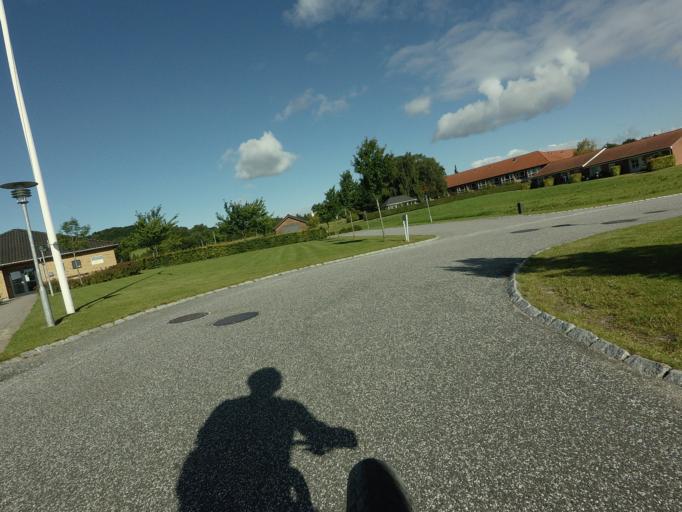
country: DK
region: Central Jutland
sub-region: Horsens Kommune
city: Horsens
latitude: 55.8969
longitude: 9.7575
